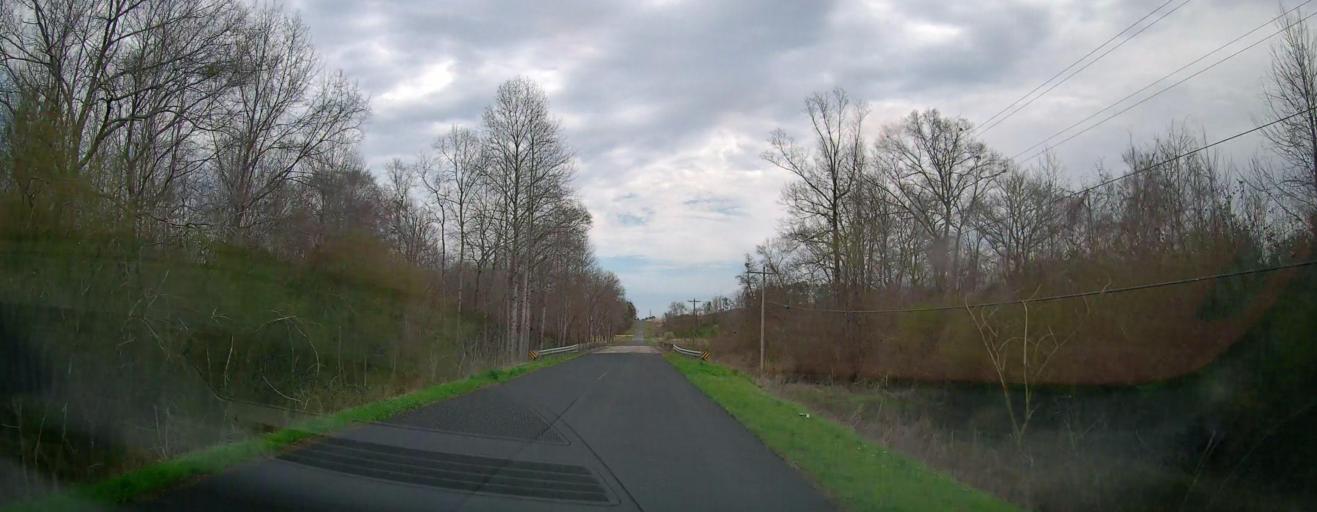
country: US
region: Alabama
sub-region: Marion County
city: Hamilton
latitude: 34.1866
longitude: -88.1407
